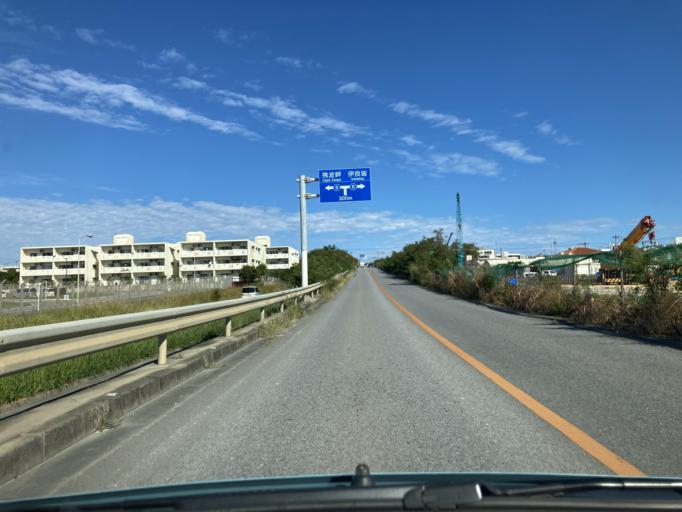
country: JP
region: Okinawa
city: Okinawa
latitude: 26.3787
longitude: 127.7455
